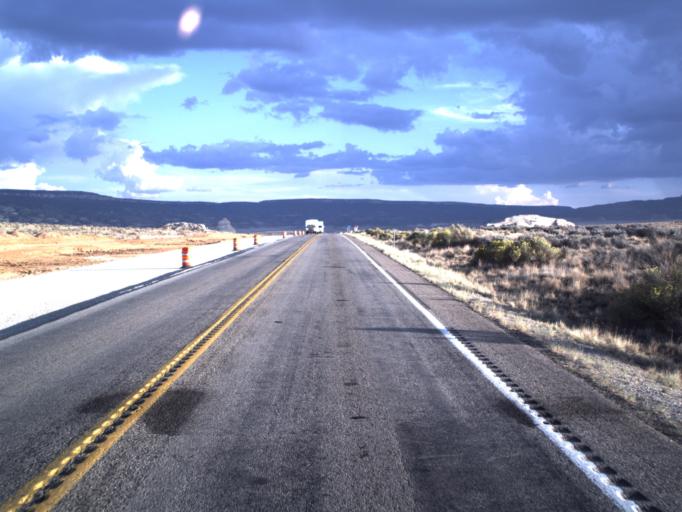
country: US
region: Utah
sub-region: San Juan County
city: Monticello
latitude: 38.1035
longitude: -109.3618
